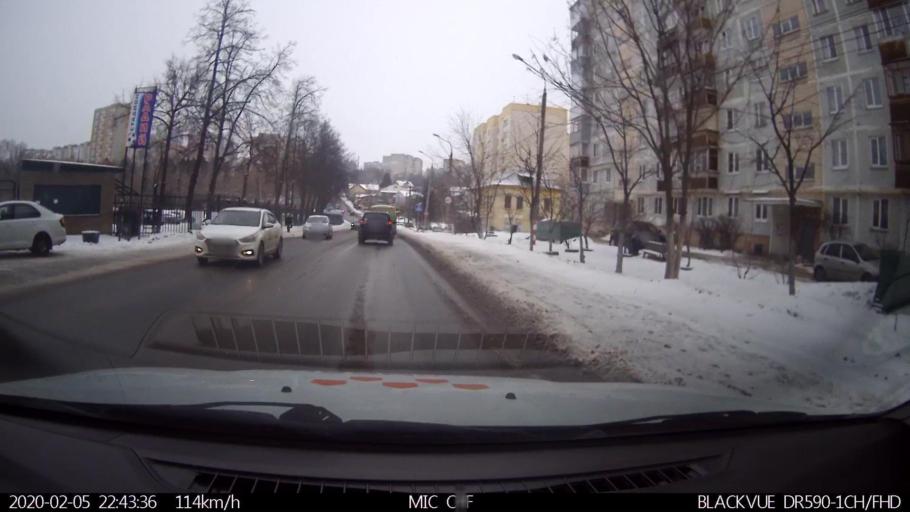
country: RU
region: Nizjnij Novgorod
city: Imeni Stepana Razina
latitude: 54.7118
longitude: 44.3819
